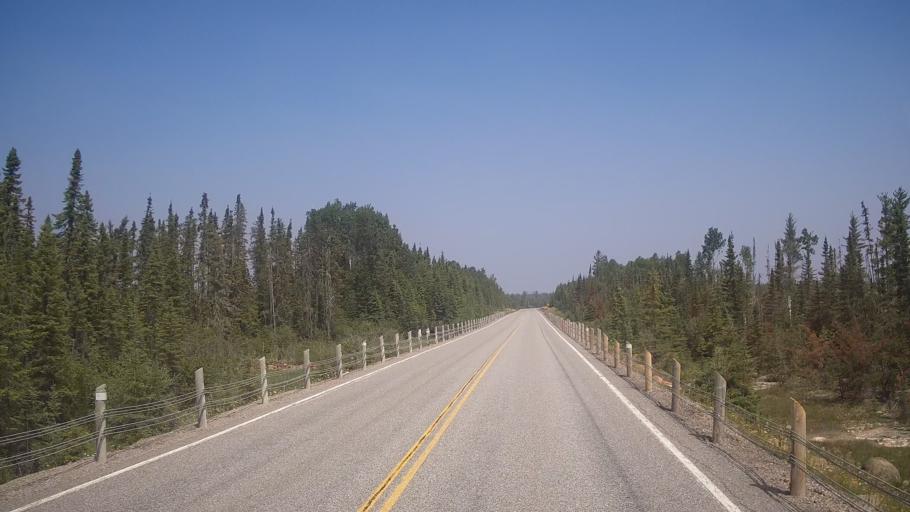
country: CA
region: Ontario
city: Timmins
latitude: 48.1846
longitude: -81.5831
